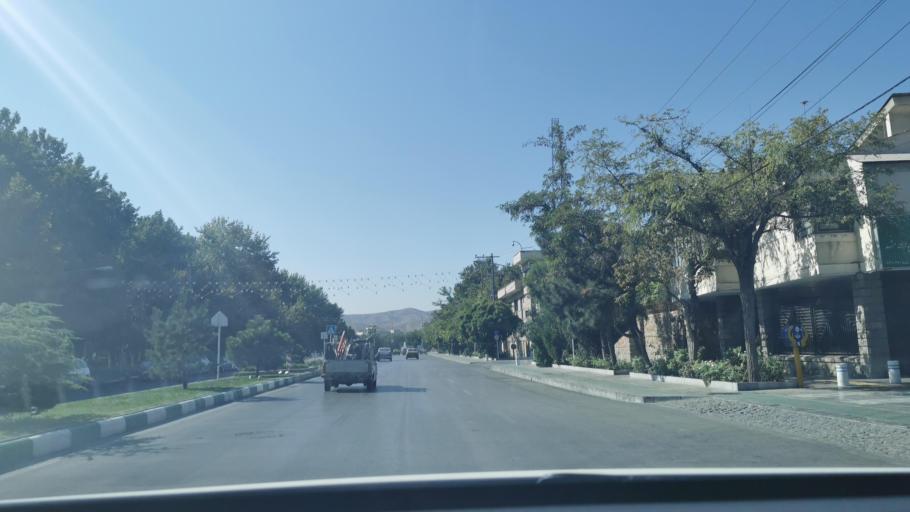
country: IR
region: Razavi Khorasan
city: Mashhad
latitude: 36.3206
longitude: 59.5330
